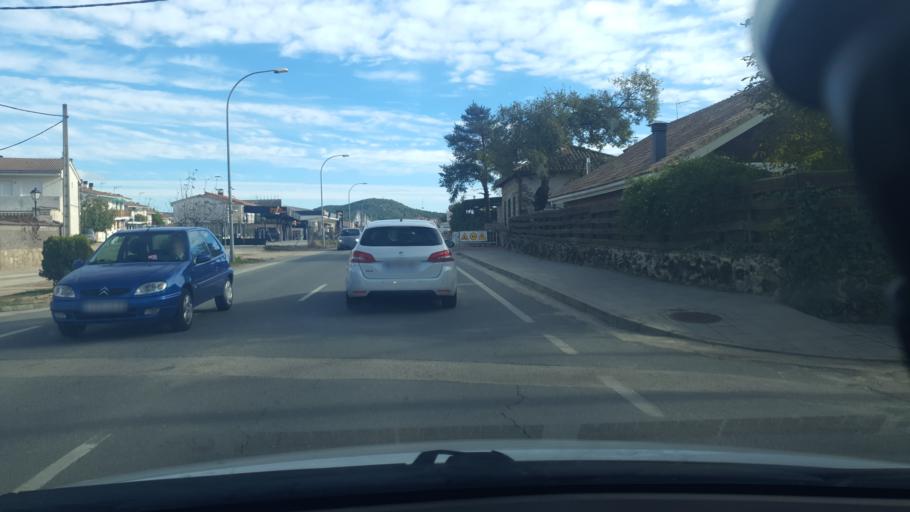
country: ES
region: Castille and Leon
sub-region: Provincia de Avila
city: La Adrada
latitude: 40.3047
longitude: -4.6439
